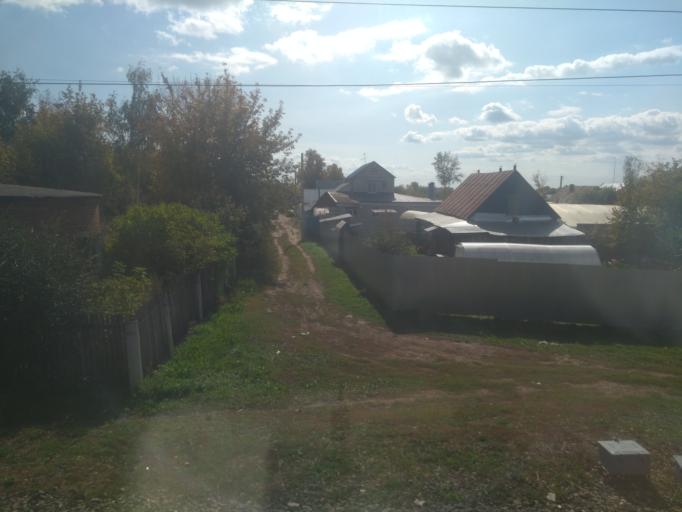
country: RU
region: Tatarstan
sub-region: Zelenodol'skiy Rayon
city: Zelenodolsk
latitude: 55.8418
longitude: 48.5729
